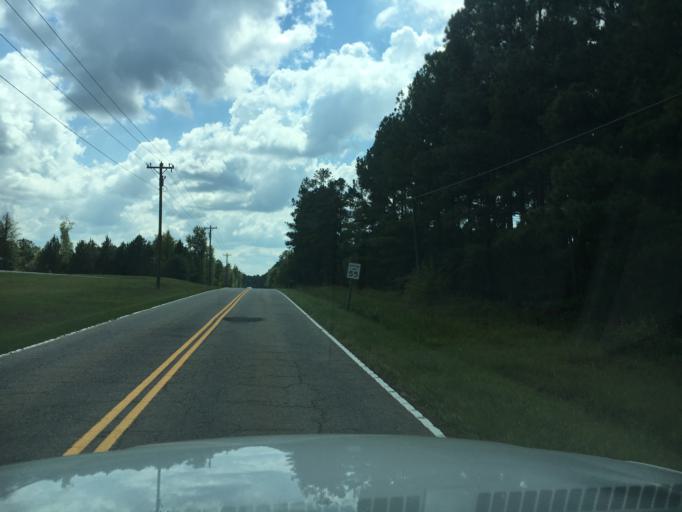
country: US
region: South Carolina
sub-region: Greenwood County
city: Greenwood
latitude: 34.1262
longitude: -82.1265
